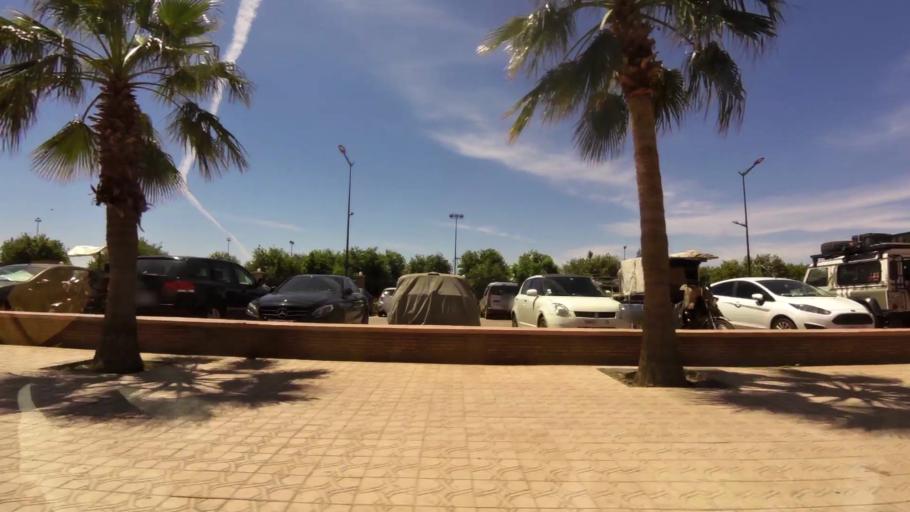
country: MA
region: Marrakech-Tensift-Al Haouz
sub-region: Marrakech
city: Marrakesh
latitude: 31.6127
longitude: -7.9897
